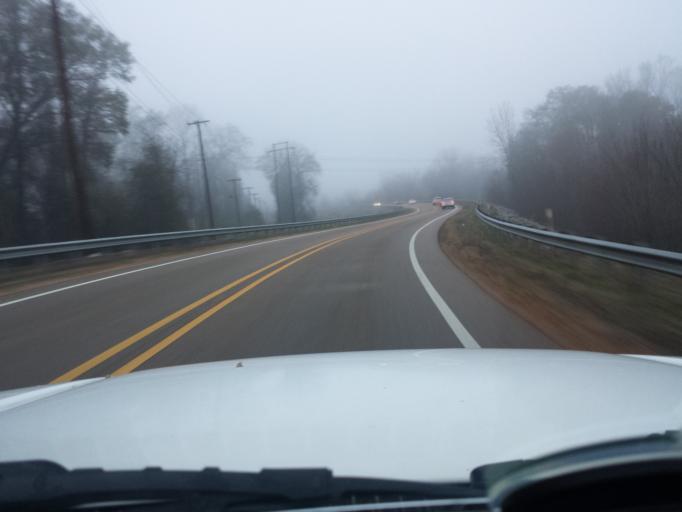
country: US
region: Mississippi
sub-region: Hinds County
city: Jackson
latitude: 32.2856
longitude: -90.1743
